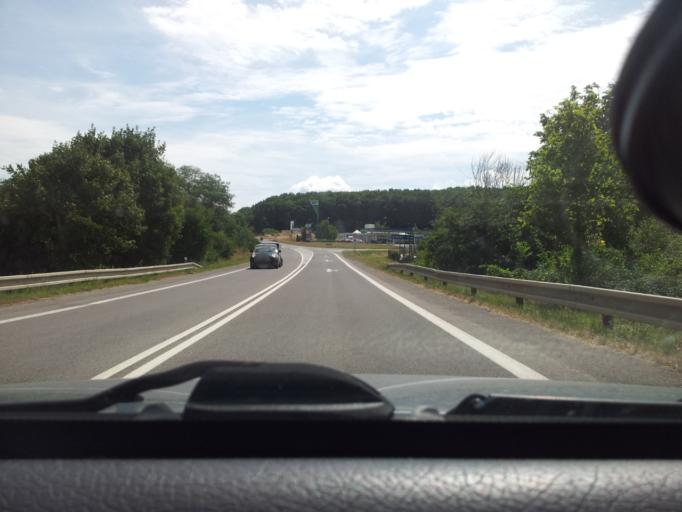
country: SK
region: Nitriansky
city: Zlate Moravce
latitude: 48.3549
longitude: 18.4773
